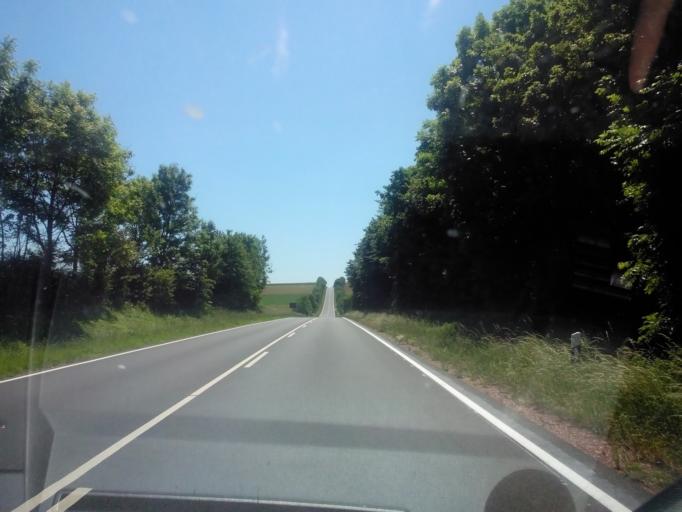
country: DE
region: Rheinland-Pfalz
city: Kirf
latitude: 49.5270
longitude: 6.4624
